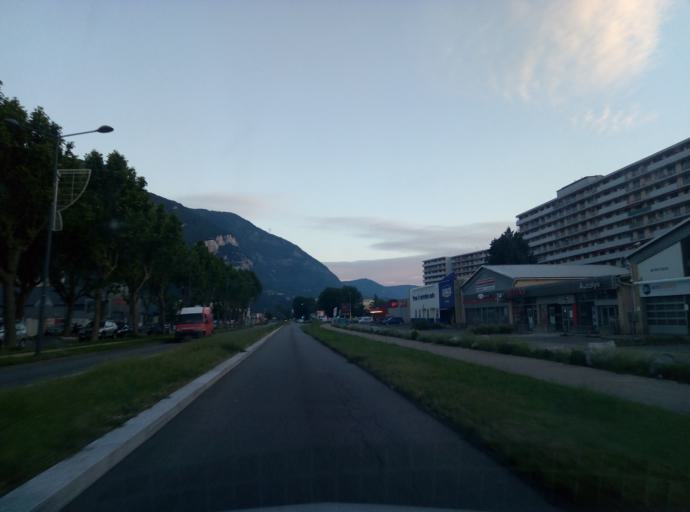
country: FR
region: Rhone-Alpes
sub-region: Departement de l'Isere
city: Fontaine
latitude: 45.1887
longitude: 5.6843
